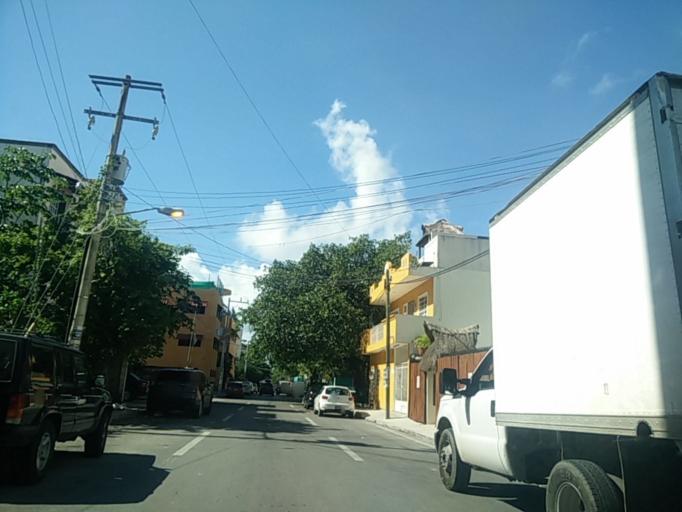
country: MX
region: Quintana Roo
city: Playa del Carmen
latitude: 20.6361
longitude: -87.0709
